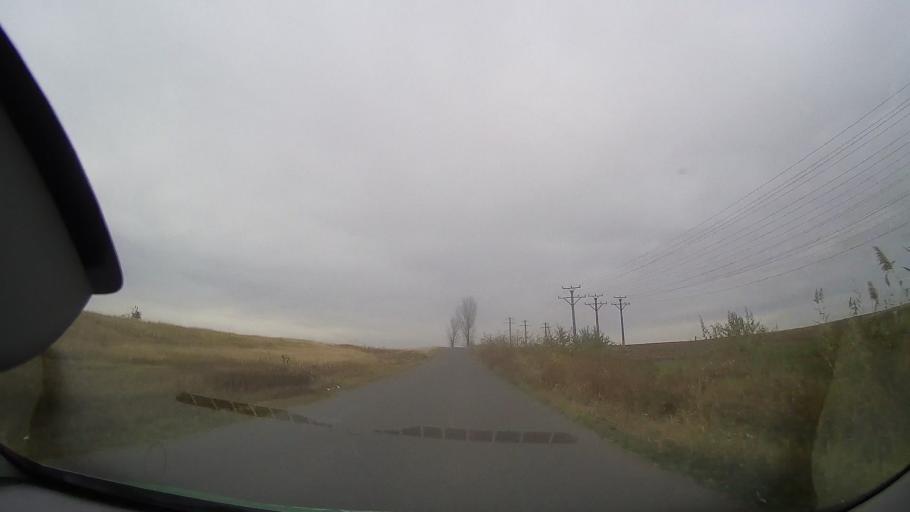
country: RO
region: Braila
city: Dudesti
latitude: 44.9053
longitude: 27.4316
